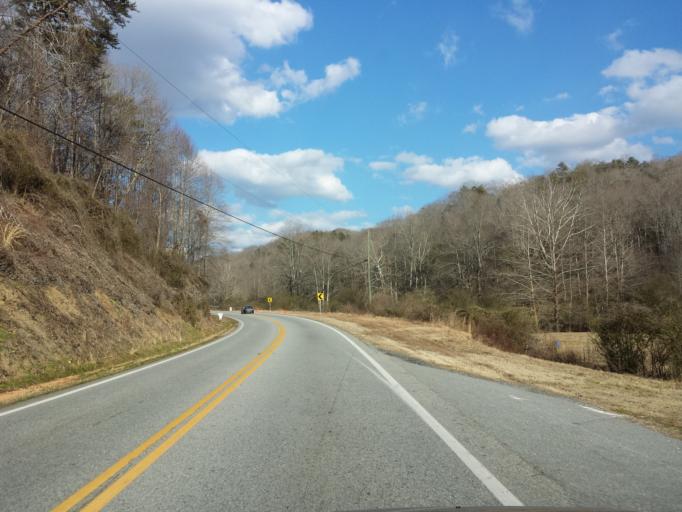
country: US
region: Georgia
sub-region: Lumpkin County
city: Dahlonega
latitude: 34.4849
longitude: -83.9531
